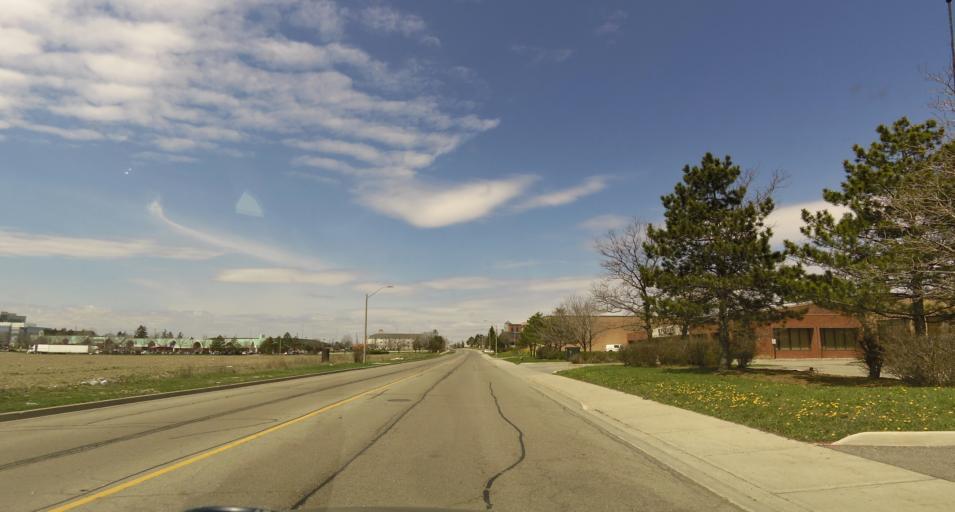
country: CA
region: Ontario
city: Mississauga
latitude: 43.6253
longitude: -79.6731
